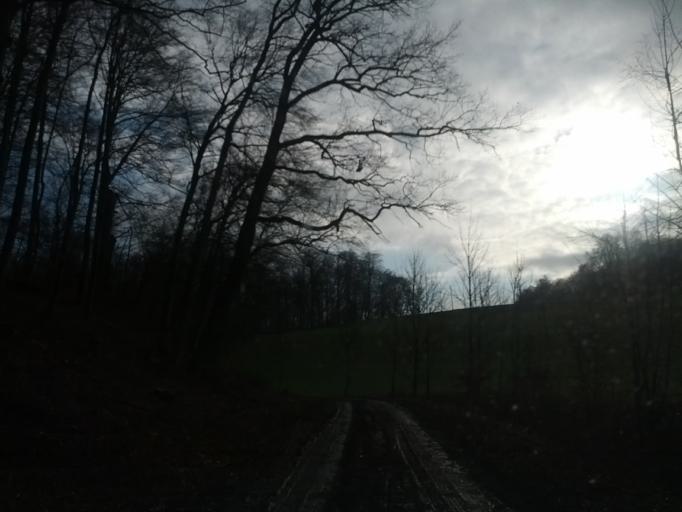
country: DE
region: Thuringia
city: Wolfsburg-Unkeroda
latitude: 50.9645
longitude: 10.2271
